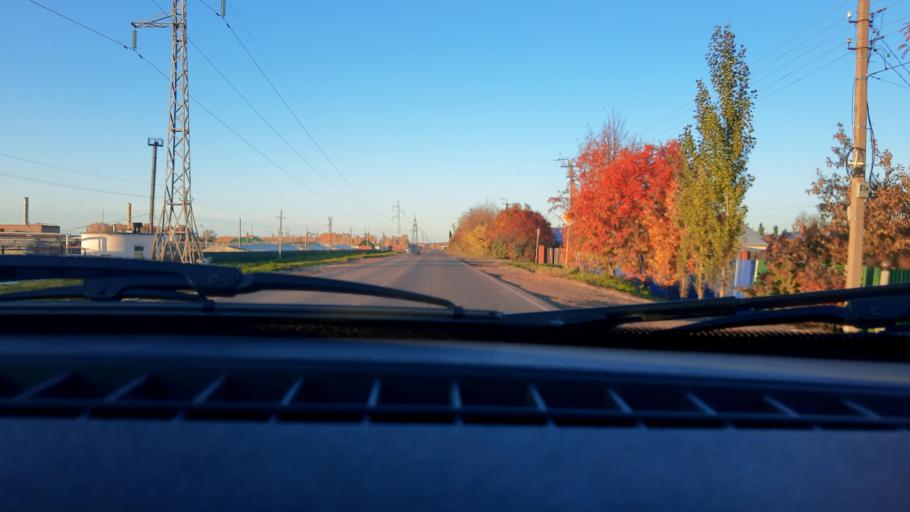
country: RU
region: Bashkortostan
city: Ufa
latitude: 54.8388
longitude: 55.9978
